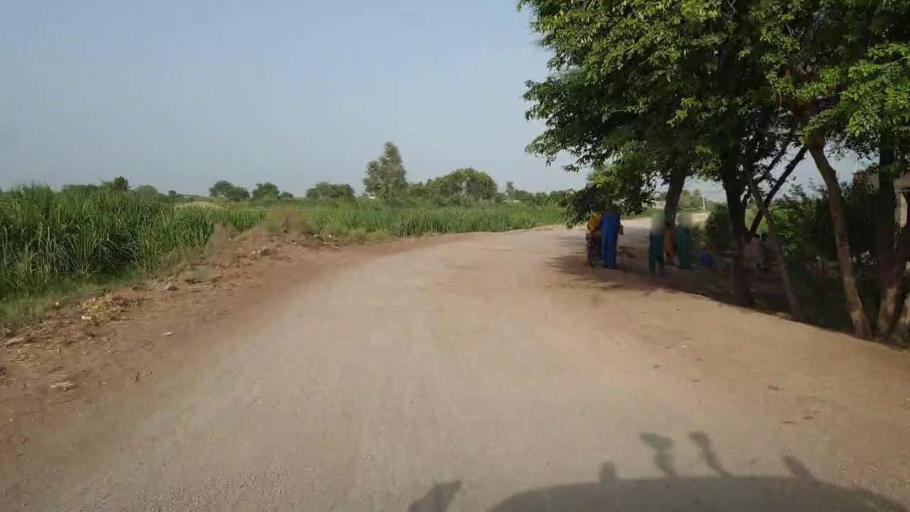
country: PK
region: Sindh
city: Daur
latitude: 26.3430
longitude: 68.2812
